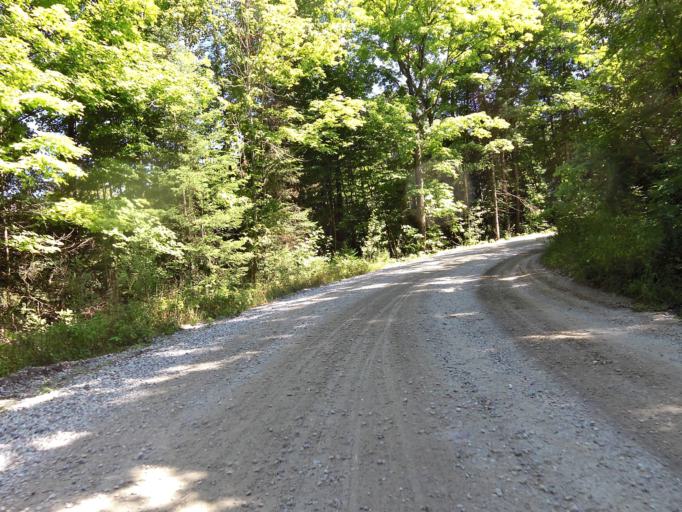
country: CA
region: Ontario
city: Renfrew
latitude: 45.1318
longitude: -76.6963
